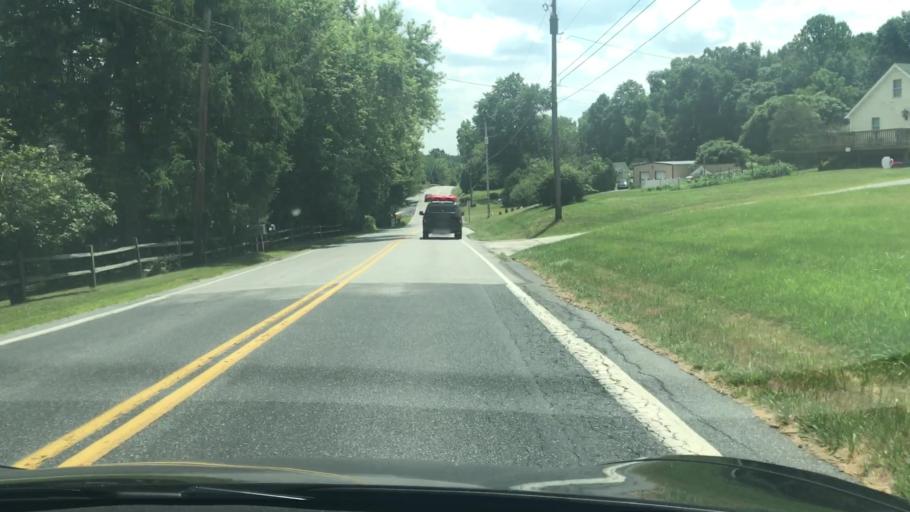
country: US
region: Pennsylvania
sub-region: York County
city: Valley Green
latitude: 40.1081
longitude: -76.7682
